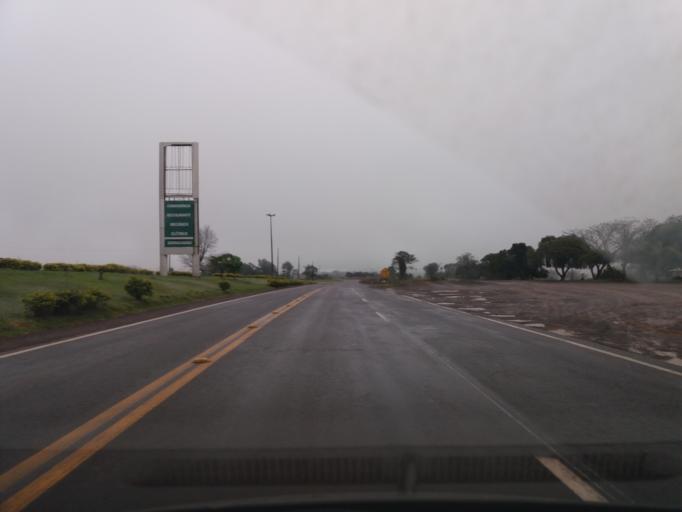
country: BR
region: Parana
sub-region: Cascavel
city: Cascavel
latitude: -25.1915
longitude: -53.6017
